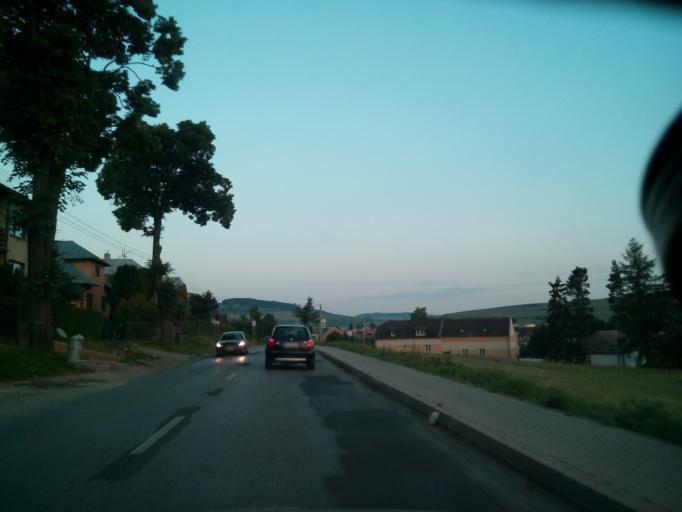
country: SK
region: Presovsky
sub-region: Okres Presov
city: Kezmarok
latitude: 49.1265
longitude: 20.4374
